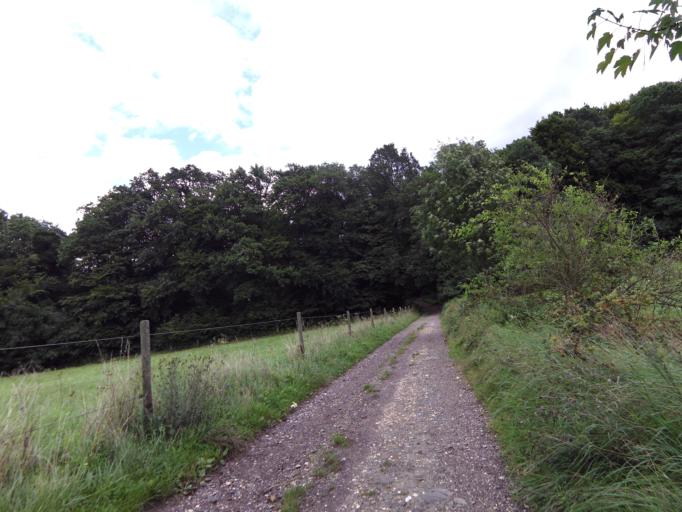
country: DE
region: Rheinland-Pfalz
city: Dernau
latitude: 50.5578
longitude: 7.0574
